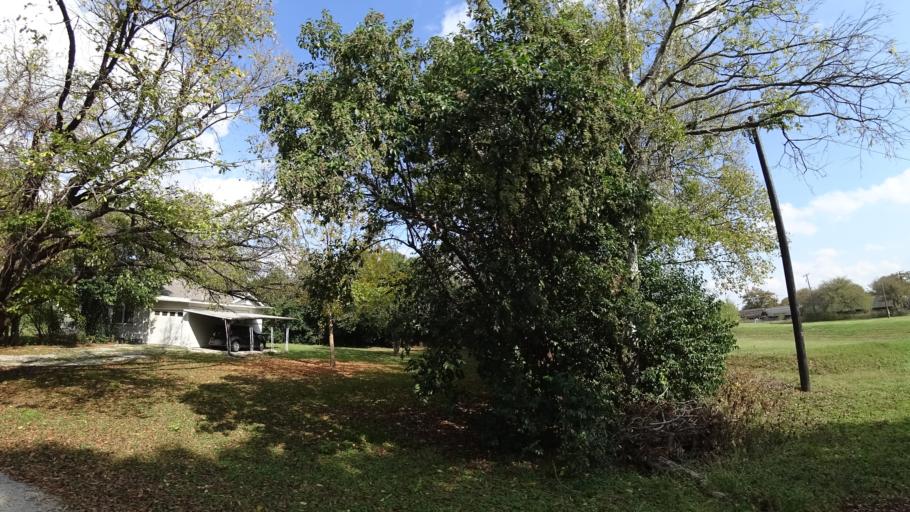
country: US
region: Texas
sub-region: Williamson County
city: Round Rock
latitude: 30.5102
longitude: -97.6712
